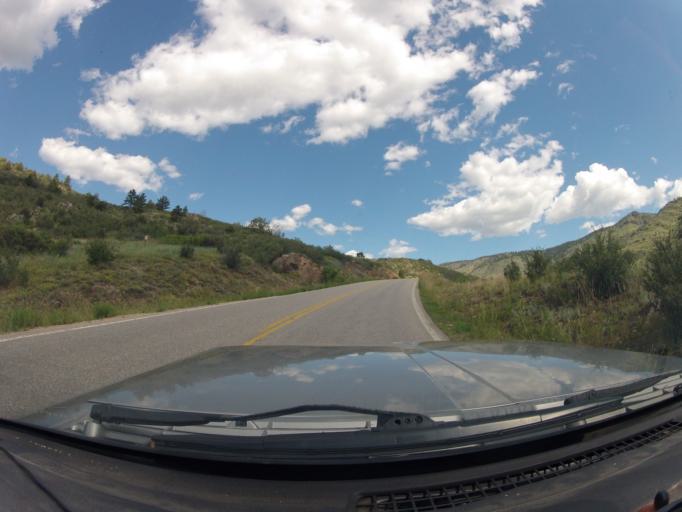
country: US
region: Colorado
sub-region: Larimer County
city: Laporte
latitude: 40.5478
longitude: -105.2875
